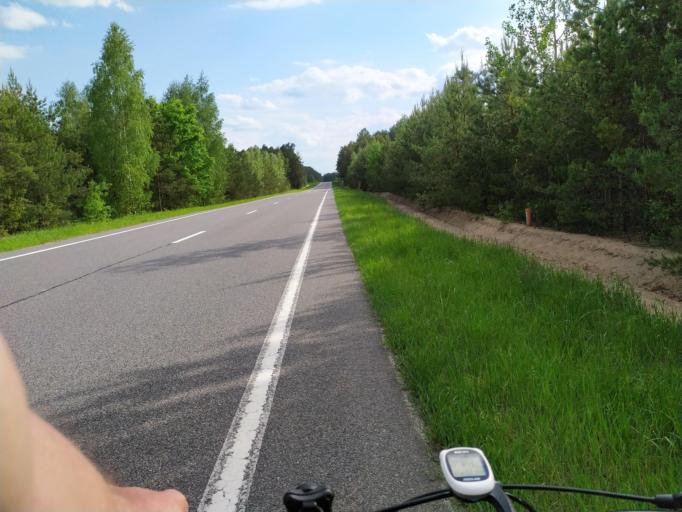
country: BY
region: Brest
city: Zhabinka
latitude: 52.4454
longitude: 24.1354
